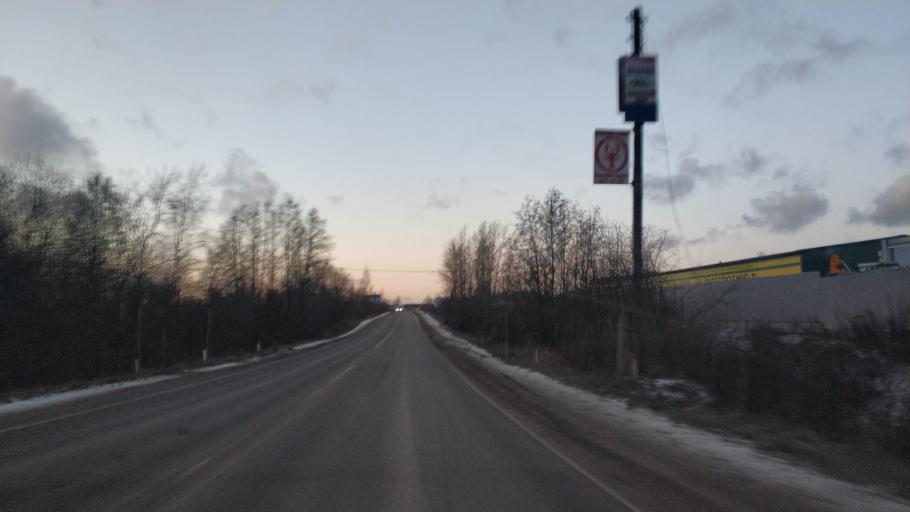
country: RU
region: St.-Petersburg
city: Pontonnyy
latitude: 59.8090
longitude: 30.6141
